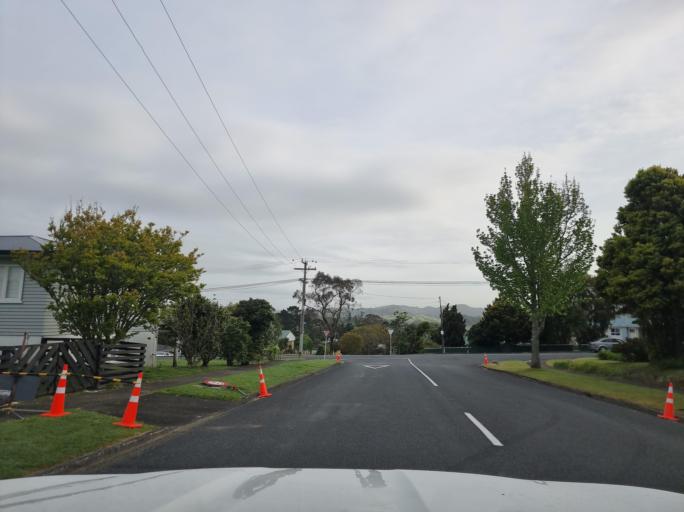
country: NZ
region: Northland
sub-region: Whangarei
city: Whangarei
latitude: -35.7494
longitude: 174.3613
